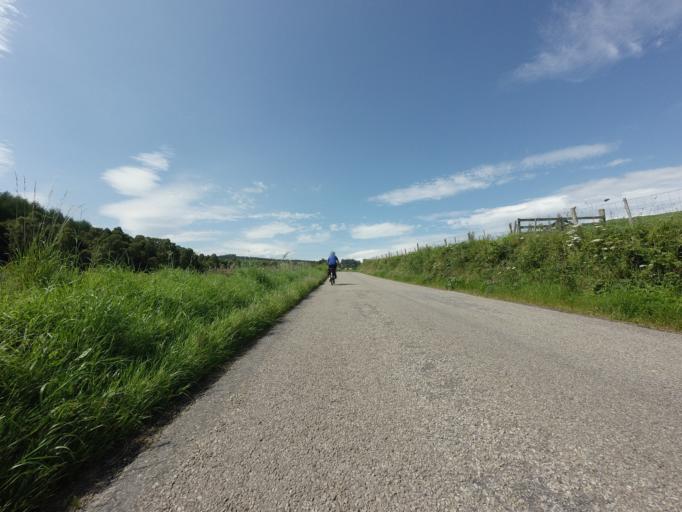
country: GB
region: Scotland
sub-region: Highland
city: Inverness
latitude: 57.5226
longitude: -4.3064
